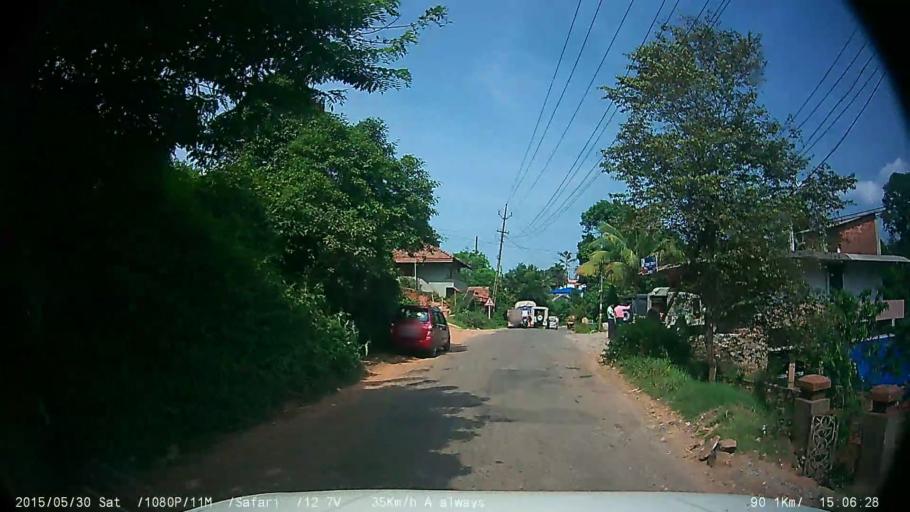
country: IN
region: Kerala
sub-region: Wayanad
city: Panamaram
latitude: 11.8019
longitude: 76.0100
